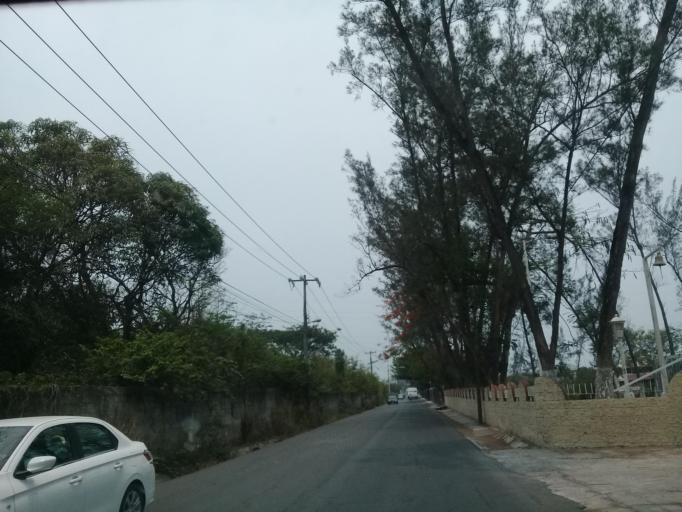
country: MX
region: Veracruz
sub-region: Veracruz
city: Las Amapolas
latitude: 19.1570
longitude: -96.2091
